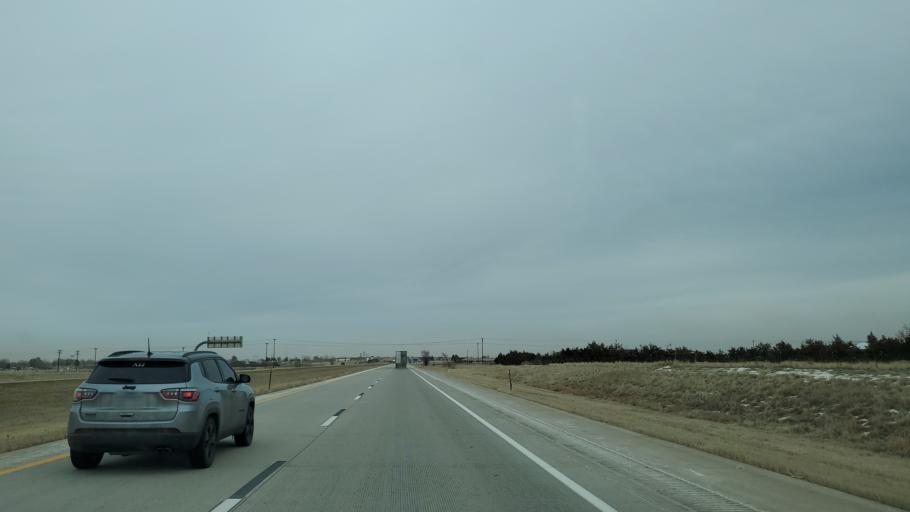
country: US
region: Colorado
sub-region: Adams County
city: Strasburg
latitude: 39.7341
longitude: -104.3445
